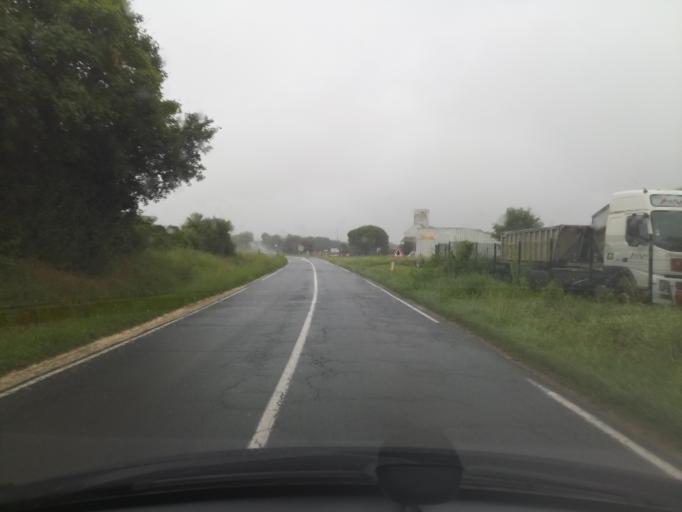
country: FR
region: Poitou-Charentes
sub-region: Departement de la Charente-Maritime
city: Saint-Jean-de-Liversay
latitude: 46.2311
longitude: -0.8804
